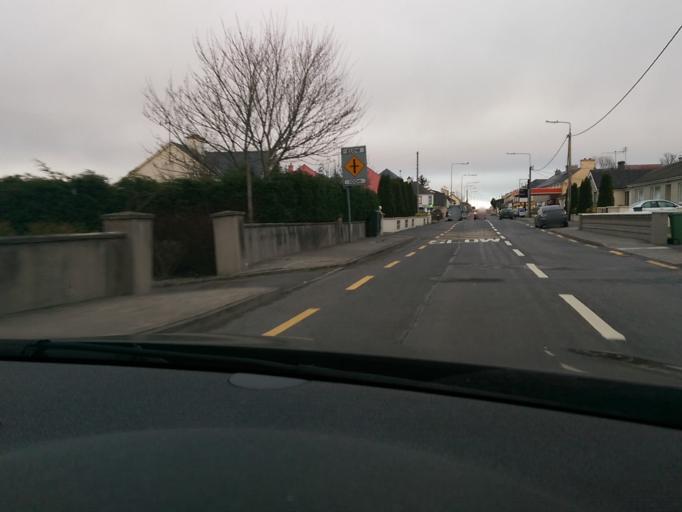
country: IE
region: Connaught
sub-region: Sligo
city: Ballymote
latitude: 53.9967
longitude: -8.5245
